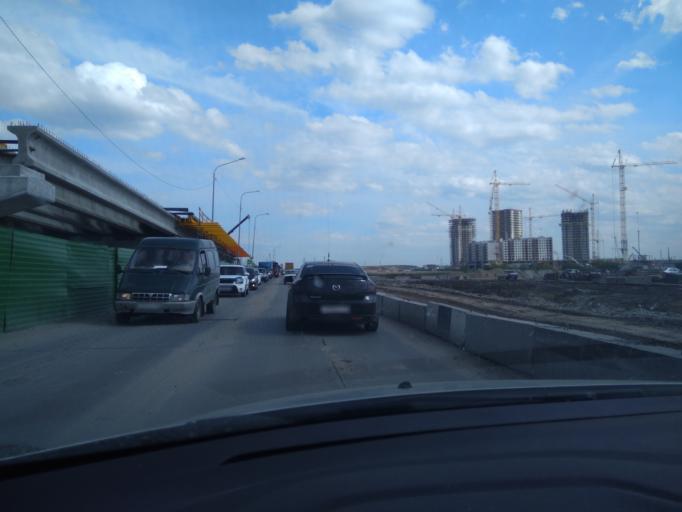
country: RU
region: Tjumen
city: Tyumen
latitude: 57.1039
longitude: 65.5641
